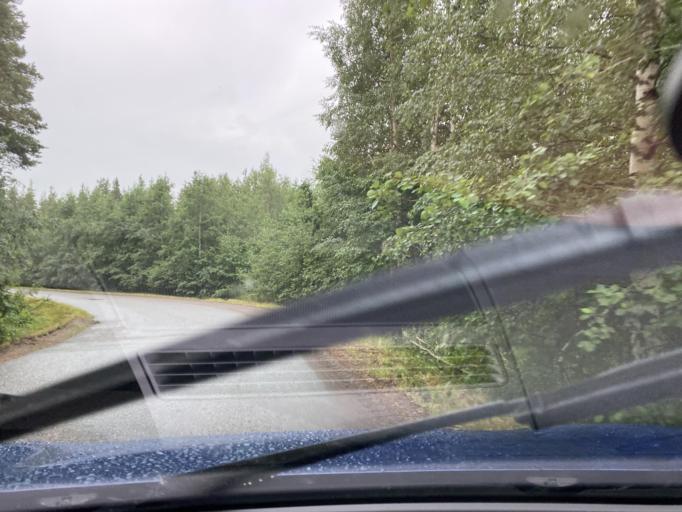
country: FI
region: Central Ostrobothnia
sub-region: Kaustinen
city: Halsua
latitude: 63.4126
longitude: 23.9733
